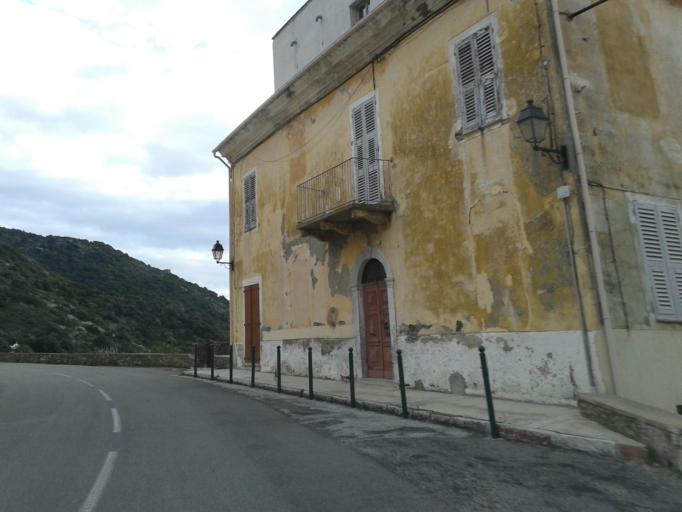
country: FR
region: Corsica
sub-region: Departement de la Haute-Corse
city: Brando
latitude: 42.8882
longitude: 9.3343
